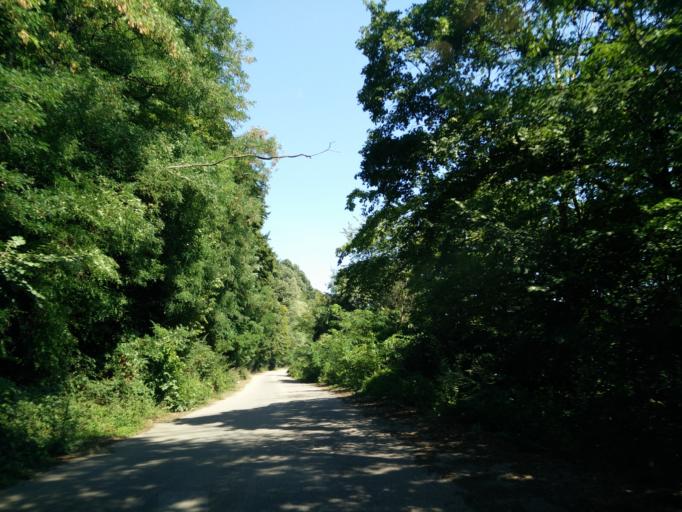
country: SK
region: Banskobystricky
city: Nova Bana
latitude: 48.4215
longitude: 18.6621
